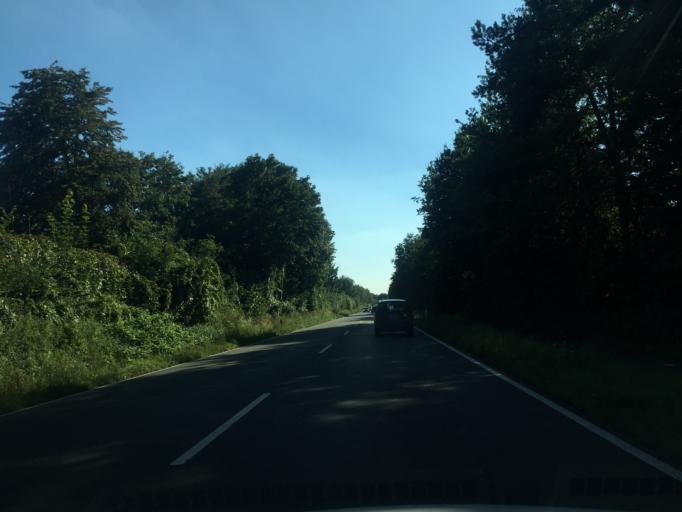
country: DE
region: North Rhine-Westphalia
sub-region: Regierungsbezirk Munster
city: Telgte
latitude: 51.9865
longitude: 7.7757
